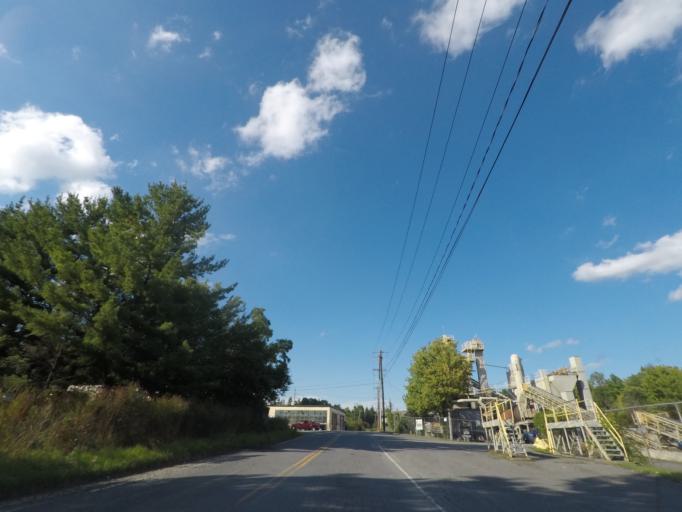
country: US
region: New York
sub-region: Albany County
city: Watervliet
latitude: 42.7426
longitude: -73.7105
